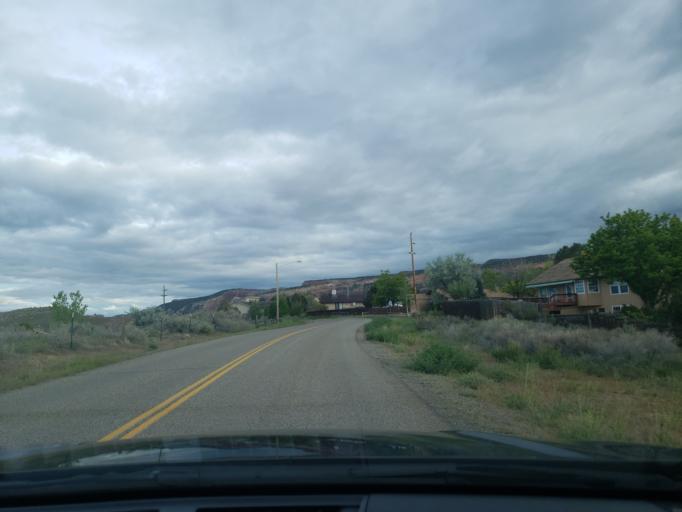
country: US
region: Colorado
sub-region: Mesa County
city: Fruita
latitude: 39.1391
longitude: -108.7421
